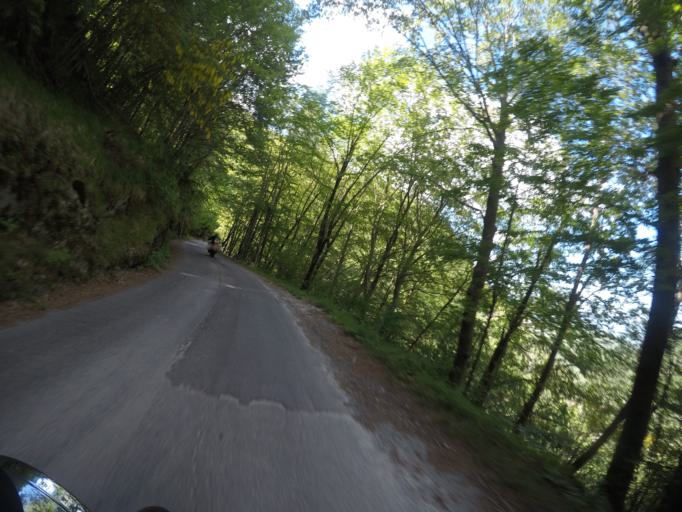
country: IT
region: Tuscany
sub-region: Provincia di Lucca
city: Minucciano
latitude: 44.1480
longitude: 10.1950
